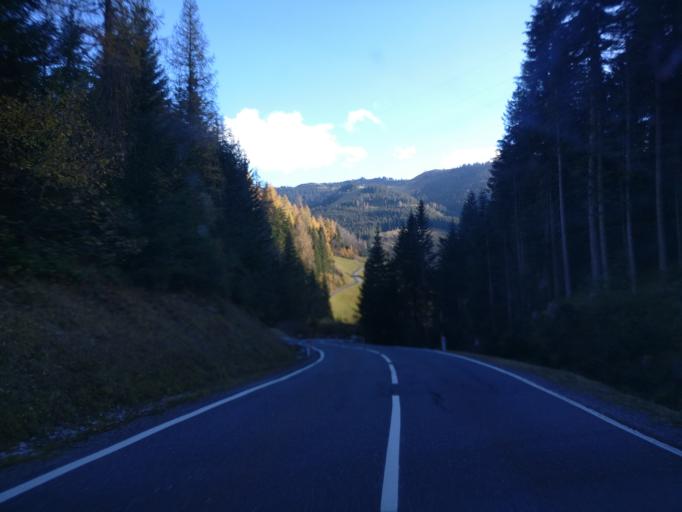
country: AT
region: Salzburg
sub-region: Politischer Bezirk Zell am See
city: Dienten am Hochkonig
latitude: 47.3958
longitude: 13.0136
